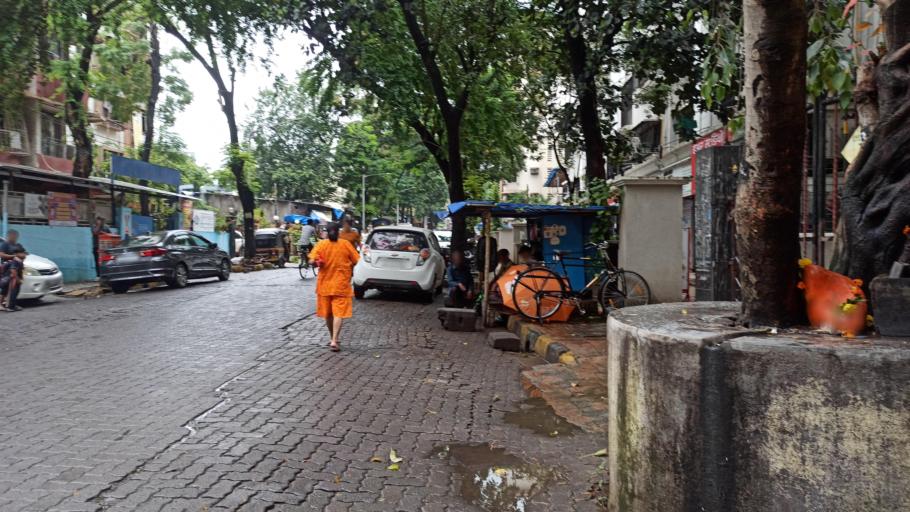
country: IN
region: Maharashtra
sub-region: Mumbai Suburban
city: Borivli
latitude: 19.2594
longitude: 72.8517
